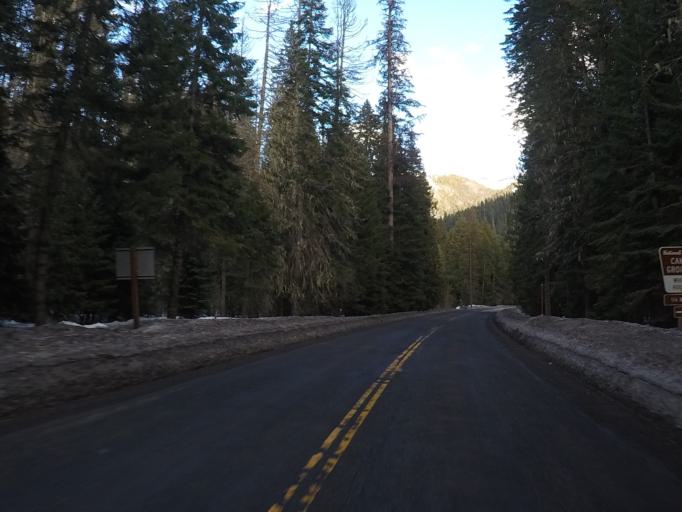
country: US
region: Montana
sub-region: Ravalli County
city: Hamilton
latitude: 46.5105
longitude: -114.7815
